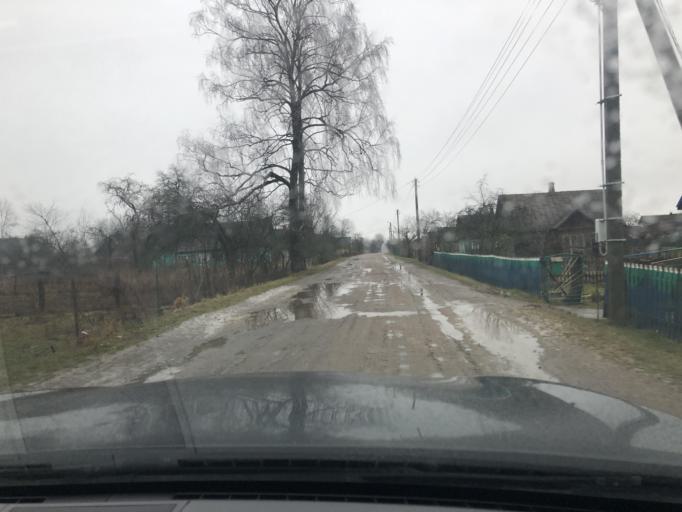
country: BY
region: Grodnenskaya
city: Hal'shany
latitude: 54.1634
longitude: 26.0896
